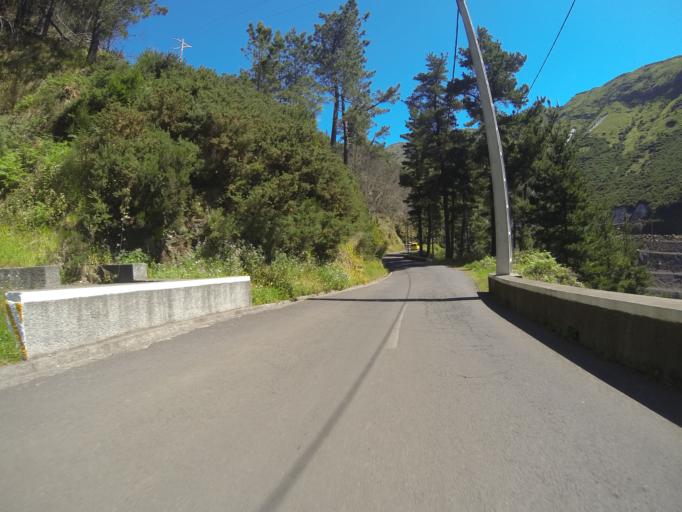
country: PT
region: Madeira
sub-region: Camara de Lobos
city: Curral das Freiras
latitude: 32.7034
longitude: -16.9550
